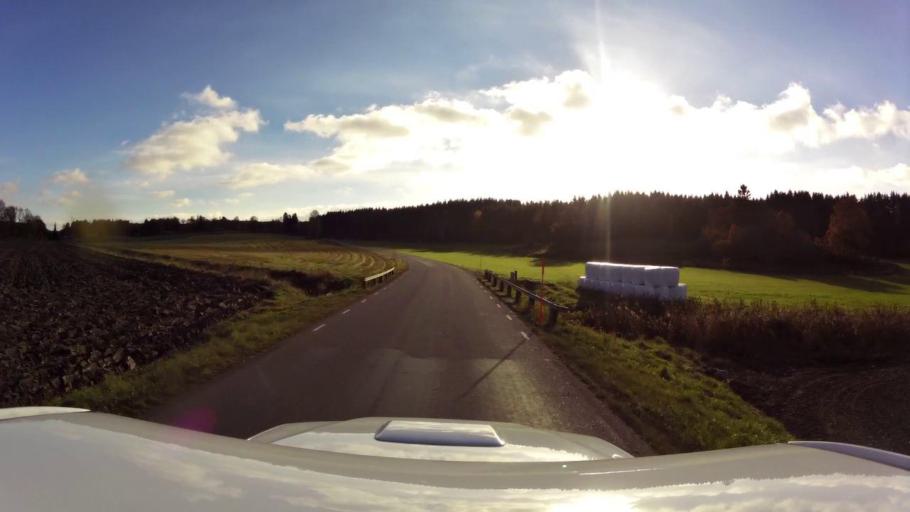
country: SE
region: OEstergoetland
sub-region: Linkopings Kommun
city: Vikingstad
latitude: 58.2786
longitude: 15.4346
